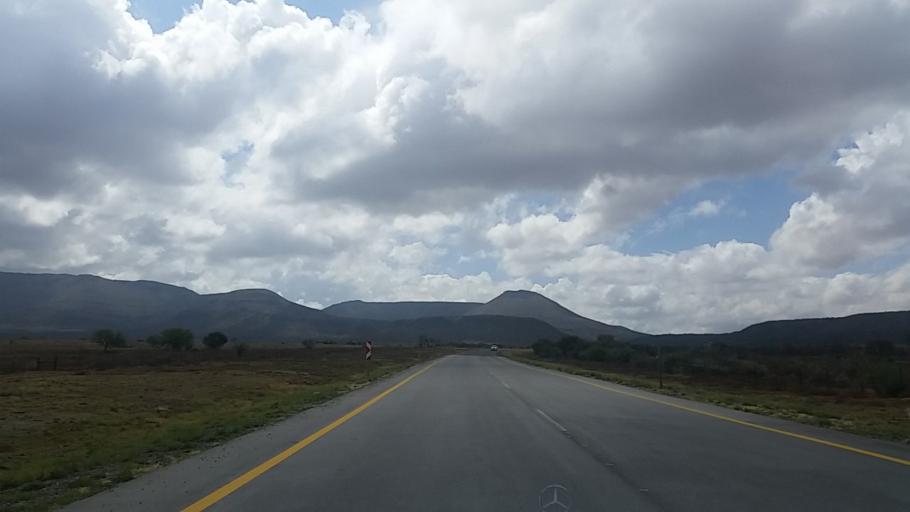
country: ZA
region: Eastern Cape
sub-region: Cacadu District Municipality
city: Graaff-Reinet
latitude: -32.0854
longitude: 24.6024
